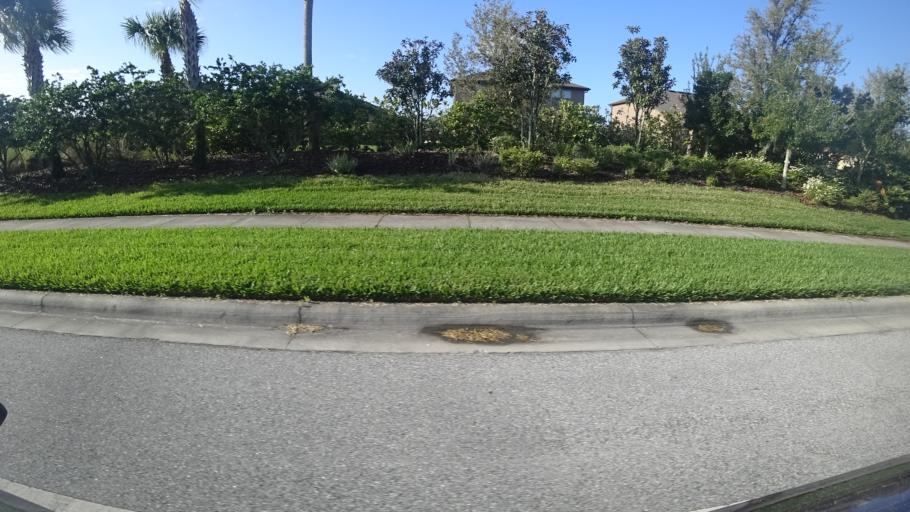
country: US
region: Florida
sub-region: Manatee County
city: Ellenton
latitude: 27.5706
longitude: -82.4668
